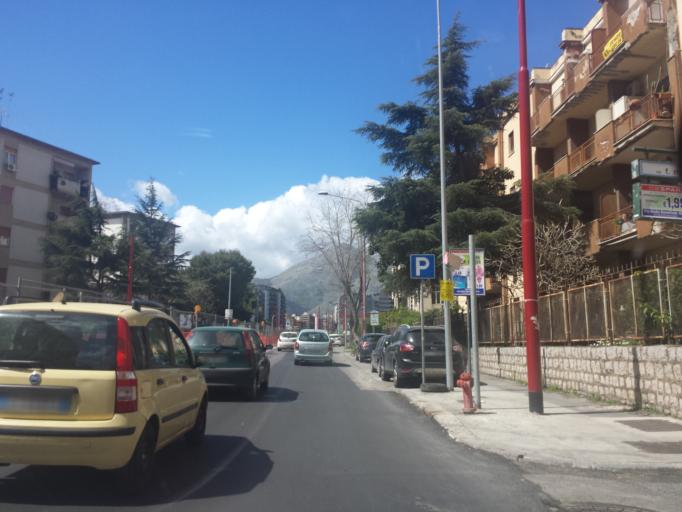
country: IT
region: Sicily
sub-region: Palermo
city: Palermo
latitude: 38.1292
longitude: 13.3320
